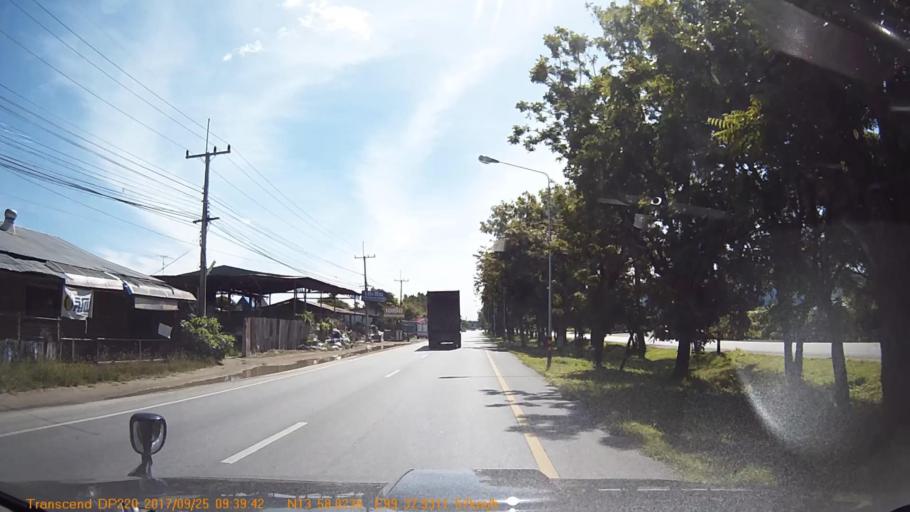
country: TH
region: Kanchanaburi
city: Tha Muang
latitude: 13.9803
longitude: 99.6326
